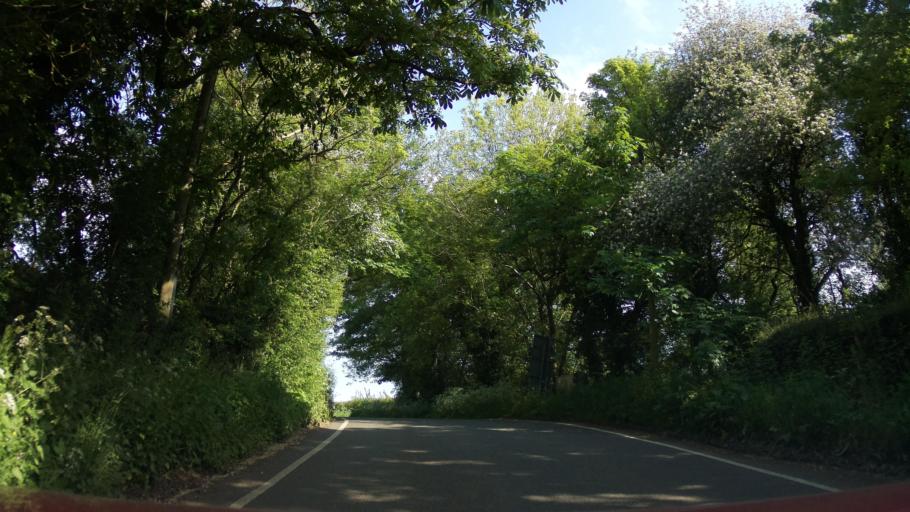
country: GB
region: England
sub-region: Wiltshire
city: Norton
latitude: 51.5573
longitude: -2.1633
